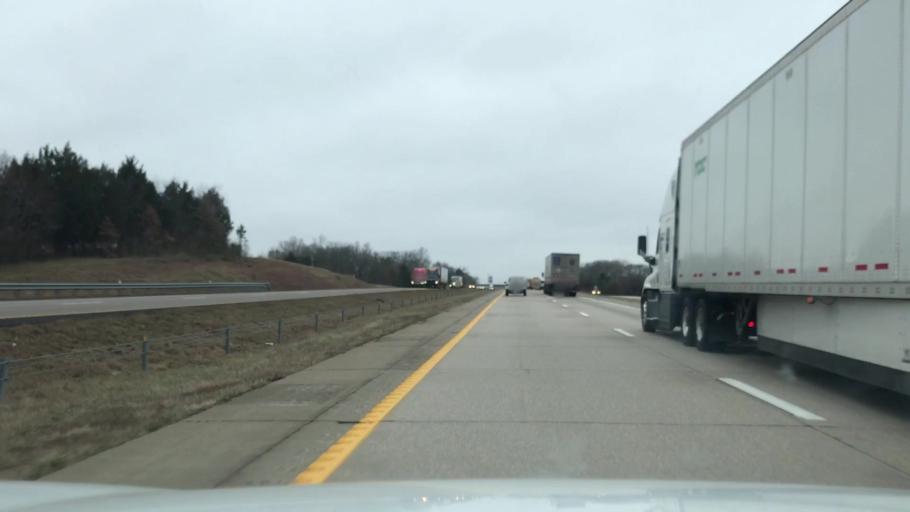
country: US
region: Missouri
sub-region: Crawford County
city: Bourbon
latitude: 38.1616
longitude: -91.2339
